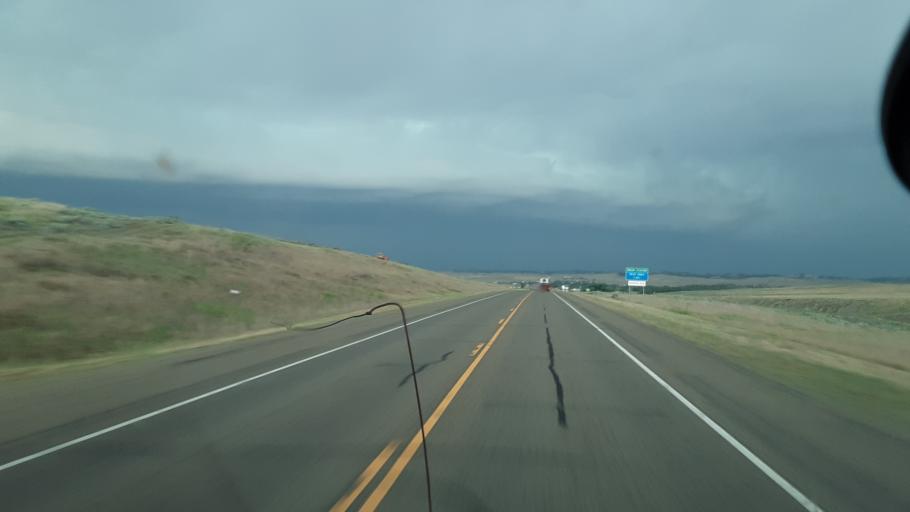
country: US
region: Montana
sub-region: Powder River County
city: Broadus
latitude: 45.4127
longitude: -105.3840
